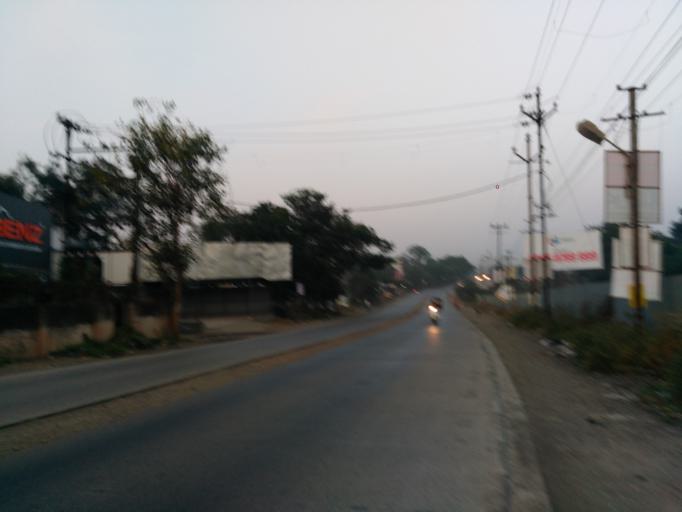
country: IN
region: Maharashtra
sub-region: Pune Division
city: Pune
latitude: 18.4512
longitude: 73.8958
